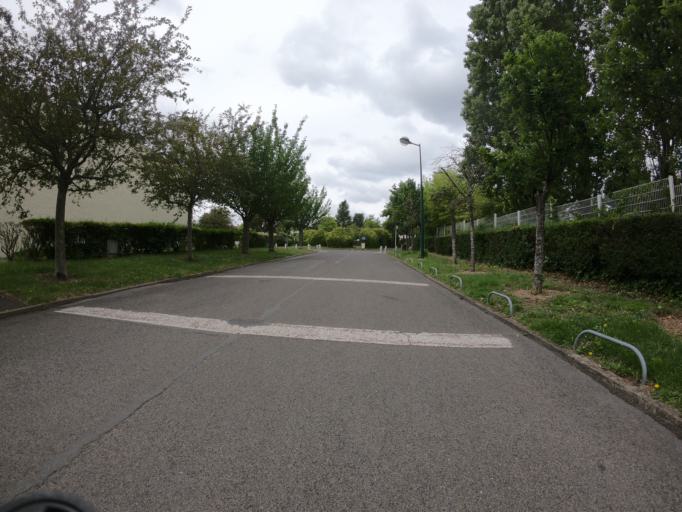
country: FR
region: Ile-de-France
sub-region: Departement des Hauts-de-Seine
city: Bourg-la-Reine
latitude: 48.7684
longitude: 2.3119
